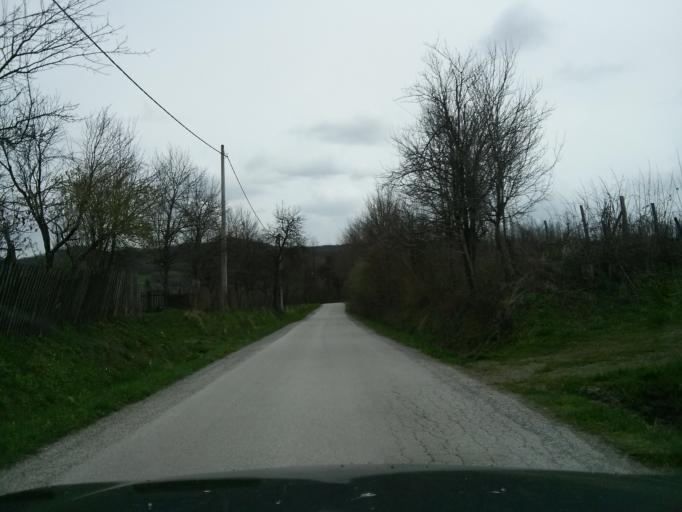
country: HR
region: Sisacko-Moslavacka
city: Gvozd
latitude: 45.2776
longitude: 15.9625
